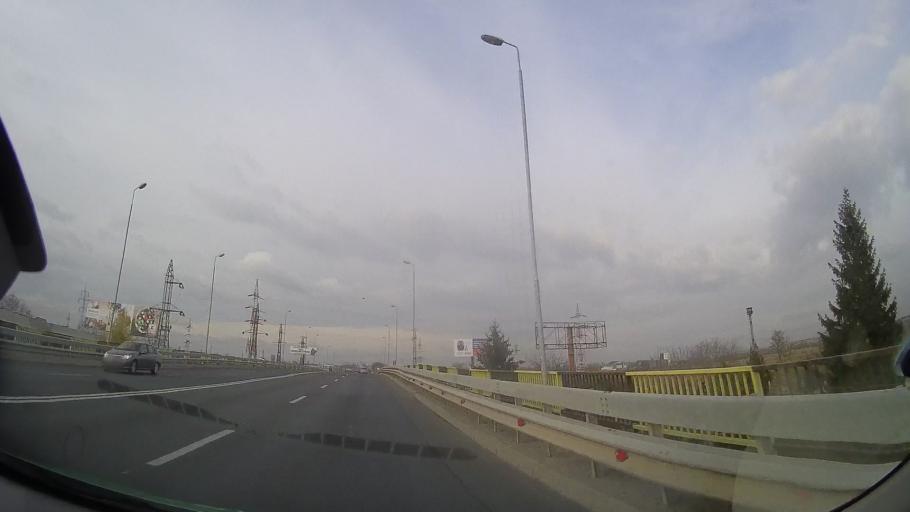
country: RO
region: Prahova
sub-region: Comuna Barcanesti
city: Tatarani
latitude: 44.9032
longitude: 26.0402
